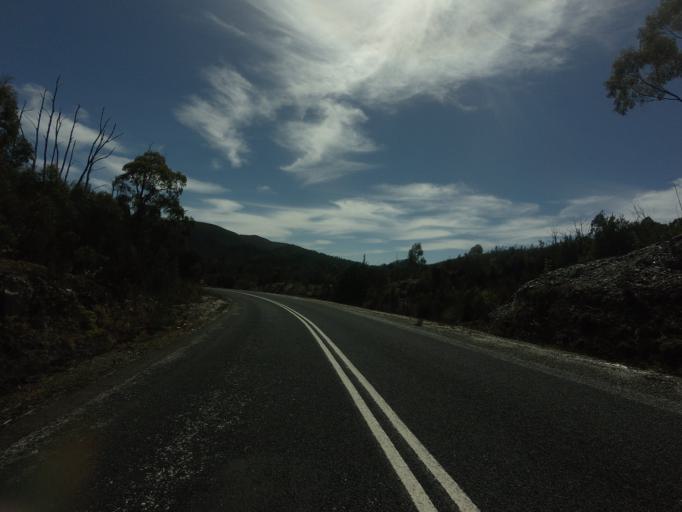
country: AU
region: Tasmania
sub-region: Huon Valley
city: Geeveston
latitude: -42.8065
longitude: 146.0971
